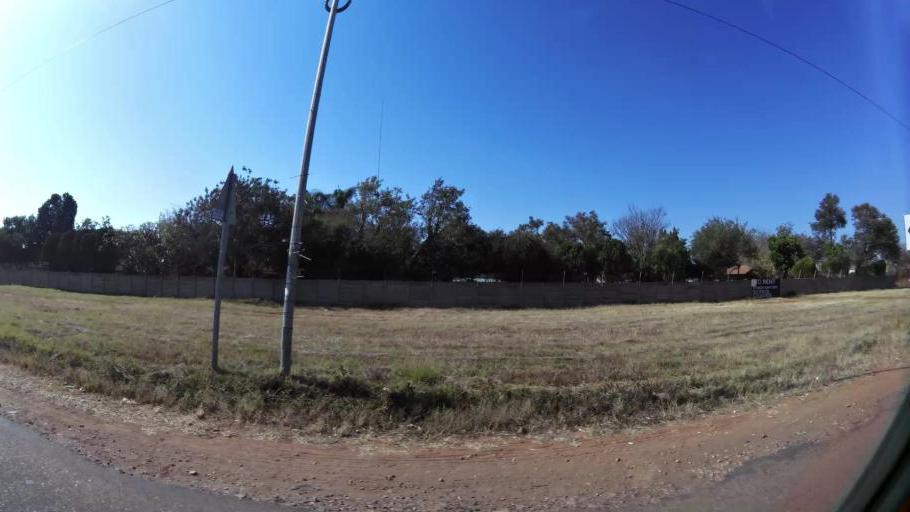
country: ZA
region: North-West
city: Ga-Rankuwa
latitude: -25.6608
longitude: 28.1017
